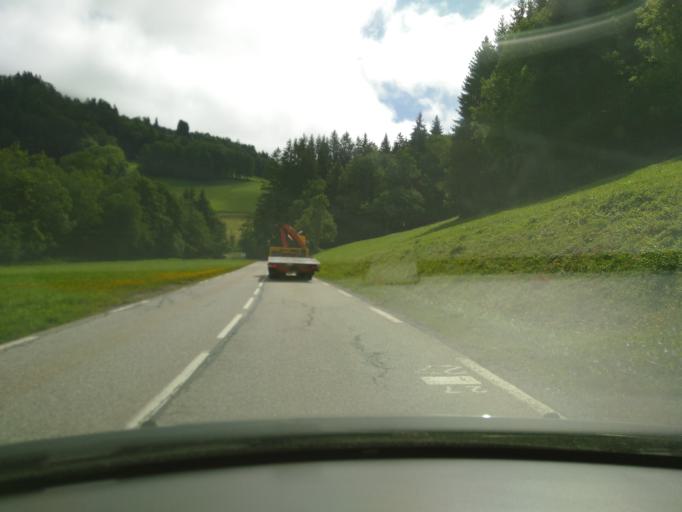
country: FR
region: Rhone-Alpes
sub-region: Departement de la Haute-Savoie
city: Saint-Jean-de-Sixt
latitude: 45.9277
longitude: 6.4079
